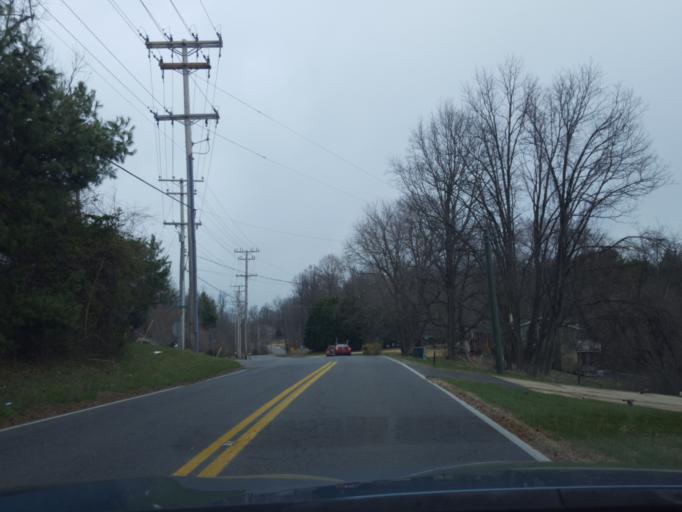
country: US
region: Maryland
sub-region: Calvert County
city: Owings
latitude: 38.7098
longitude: -76.5718
